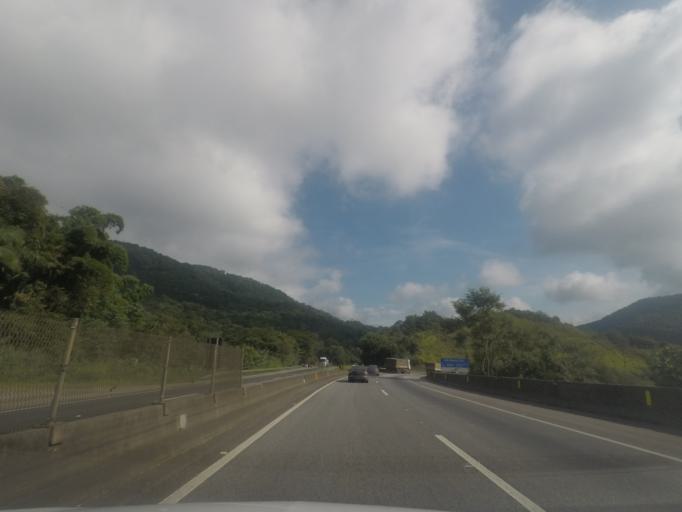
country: BR
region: Parana
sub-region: Antonina
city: Antonina
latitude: -25.5653
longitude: -48.8122
